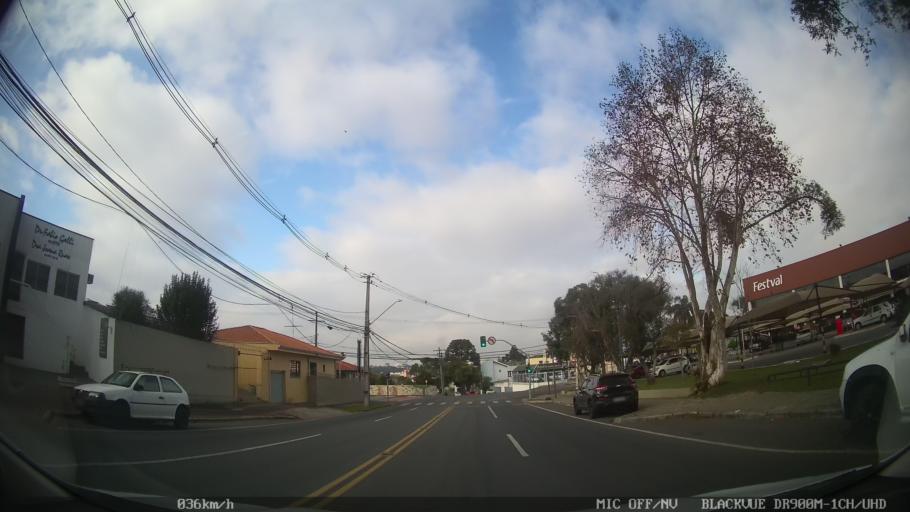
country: BR
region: Parana
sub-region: Curitiba
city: Curitiba
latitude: -25.4024
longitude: -49.3346
